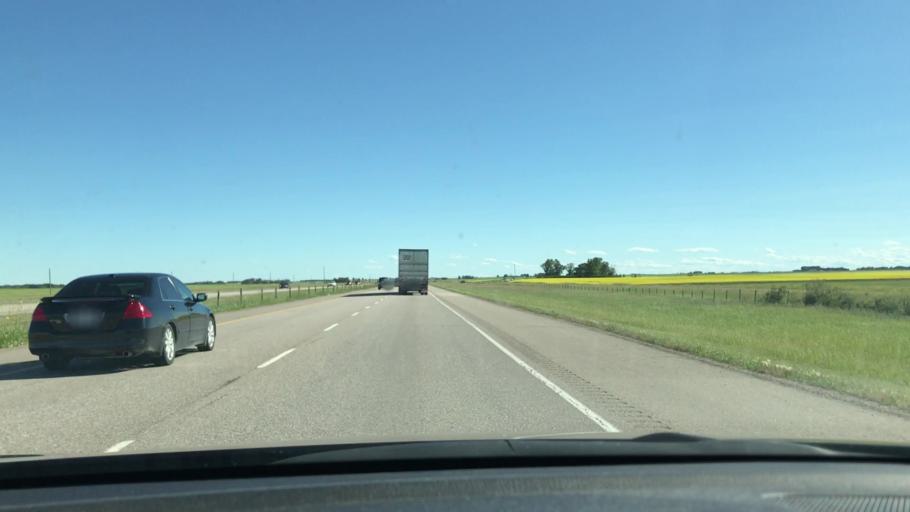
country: CA
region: Alberta
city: Olds
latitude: 51.7177
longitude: -114.0256
